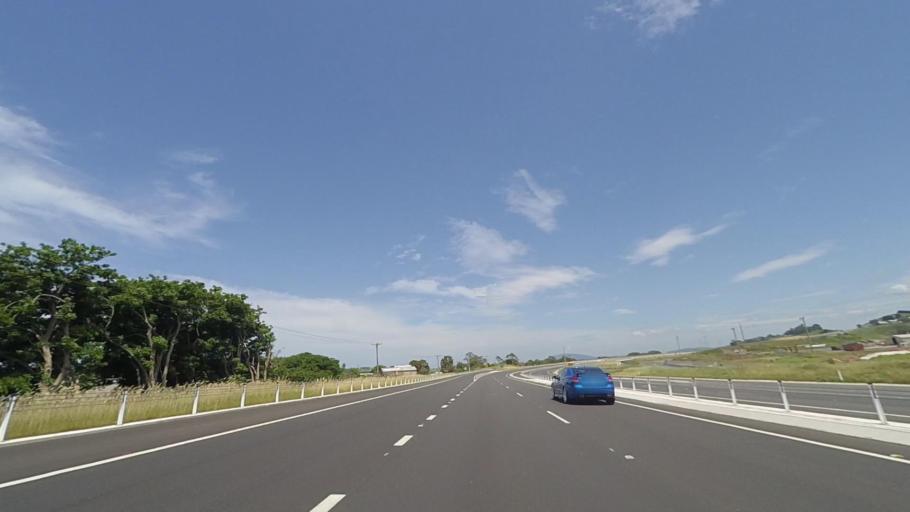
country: AU
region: New South Wales
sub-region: Kiama
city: Gerringong
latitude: -34.7423
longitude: 150.8194
